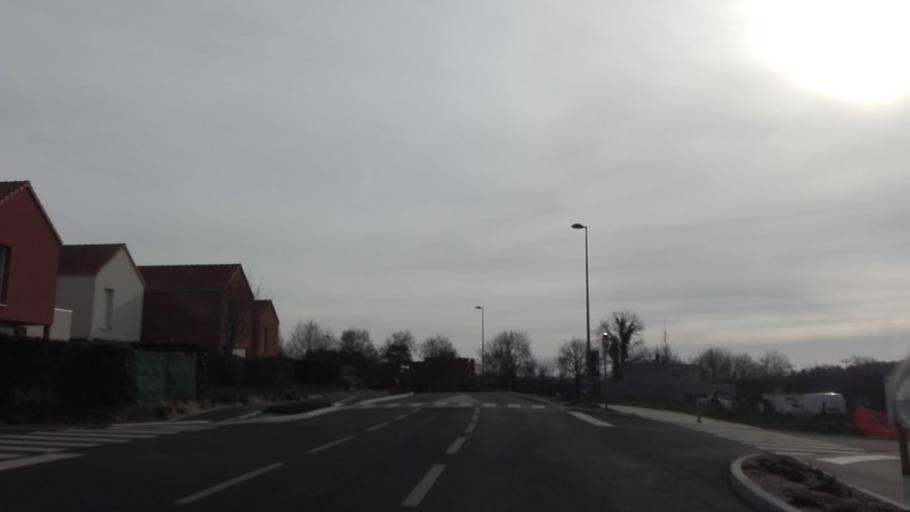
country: FR
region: Pays de la Loire
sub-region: Departement de la Vendee
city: Les Herbiers
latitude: 46.8806
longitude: -1.0150
